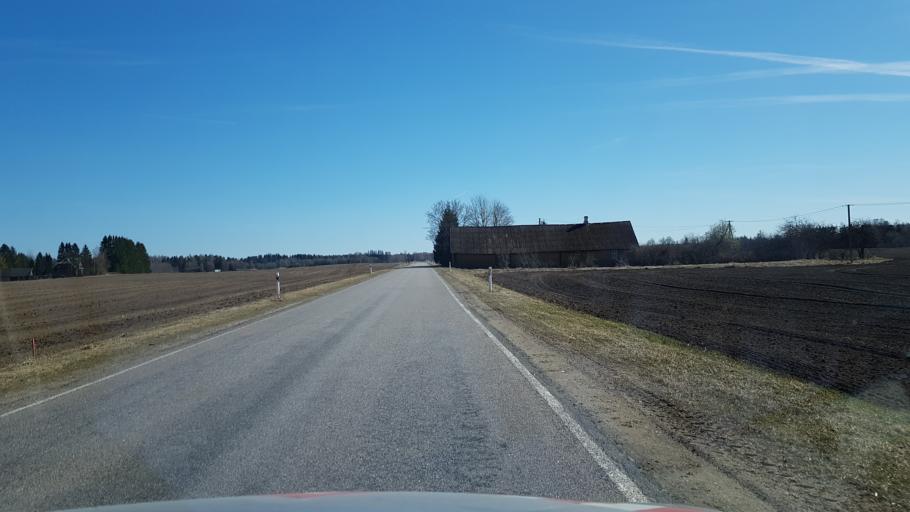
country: EE
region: Laeaene-Virumaa
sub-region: Vinni vald
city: Vinni
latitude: 59.2439
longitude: 26.6904
